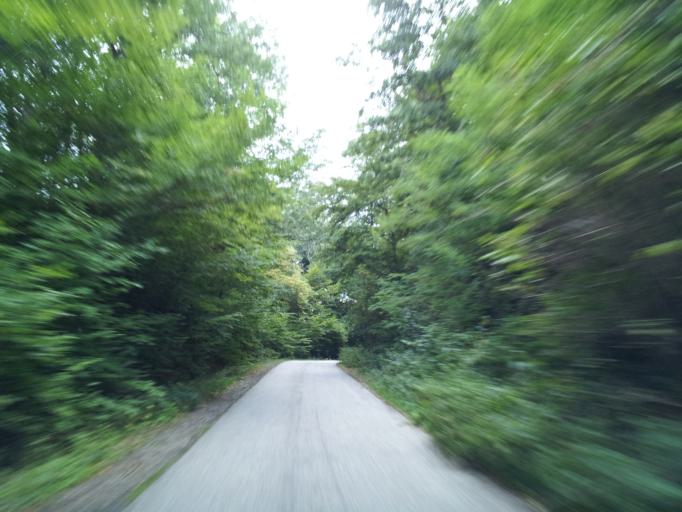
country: HU
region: Pest
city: Kismaros
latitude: 47.8859
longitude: 18.9799
